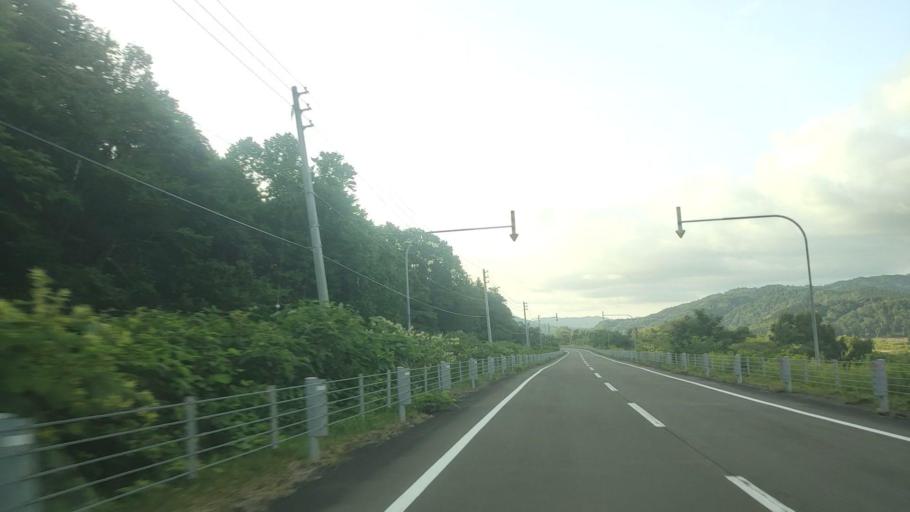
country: JP
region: Hokkaido
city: Bibai
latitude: 43.0753
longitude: 142.1022
